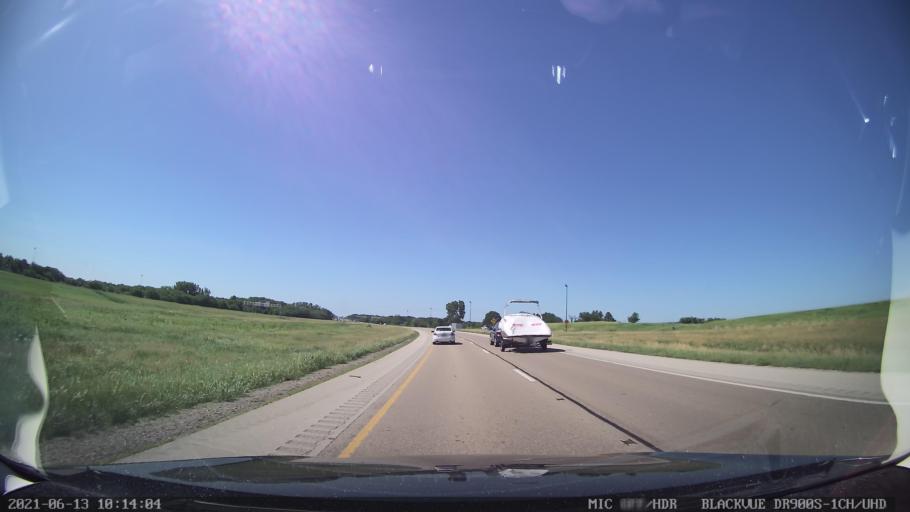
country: US
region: Illinois
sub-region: Logan County
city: Lincoln
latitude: 40.1758
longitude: -89.4176
